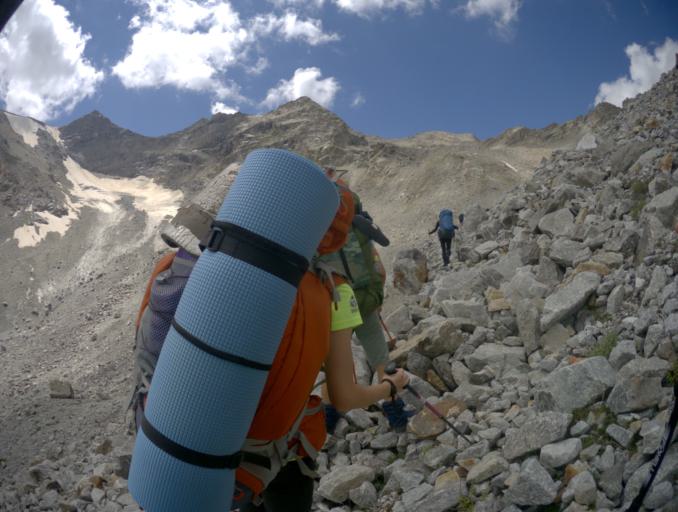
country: RU
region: Karachayevo-Cherkesiya
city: Uchkulan
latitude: 43.3220
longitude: 42.0866
